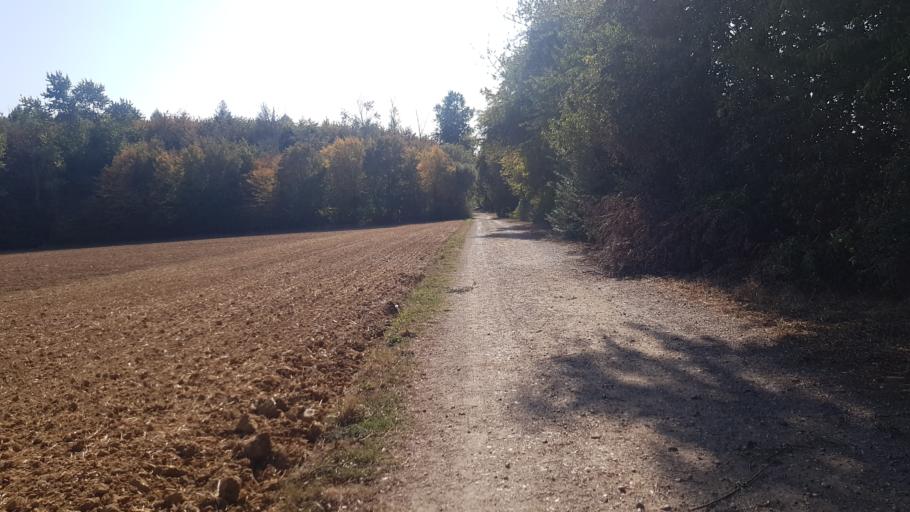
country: DE
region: North Rhine-Westphalia
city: Niedermerz
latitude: 50.8743
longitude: 6.2552
